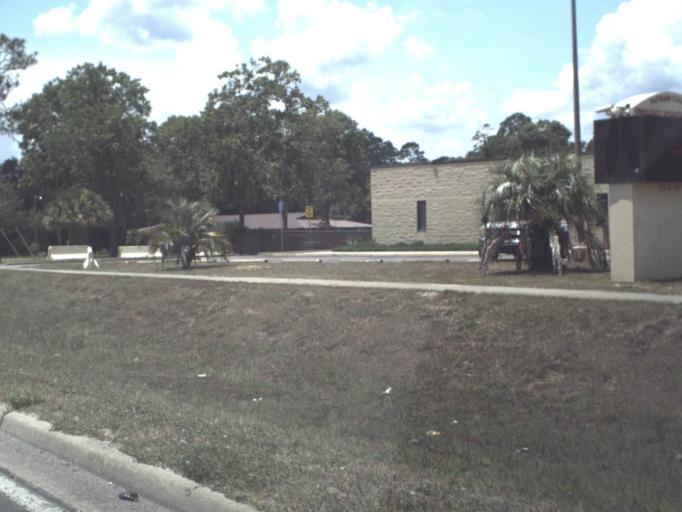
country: US
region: Florida
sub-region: Putnam County
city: Palatka
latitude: 29.6449
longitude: -81.6750
